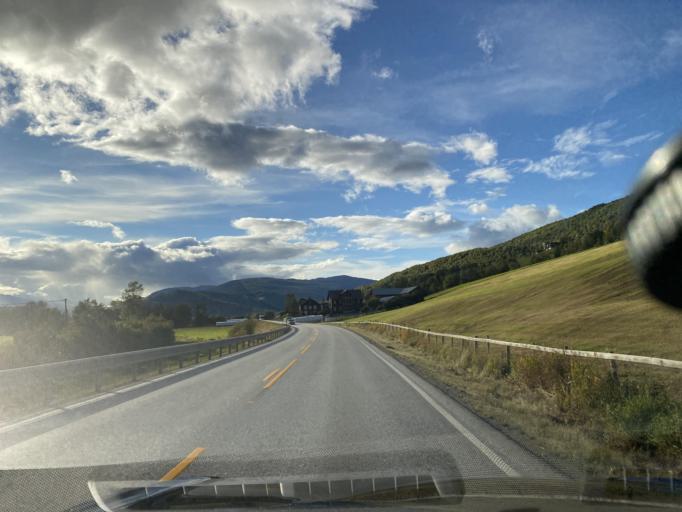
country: NO
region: Oppland
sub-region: Vaga
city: Vagamo
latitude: 61.8754
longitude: 9.1534
